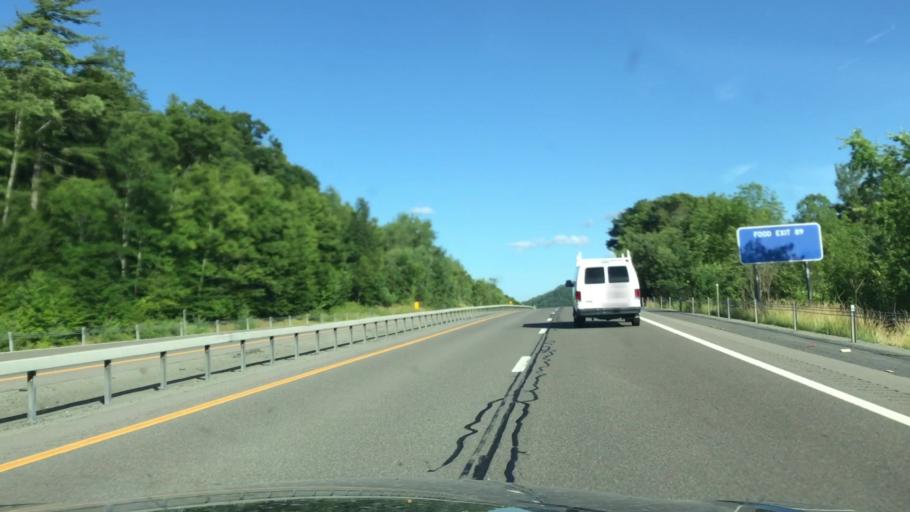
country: US
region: New York
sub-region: Delaware County
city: Hancock
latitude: 41.9748
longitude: -75.1950
